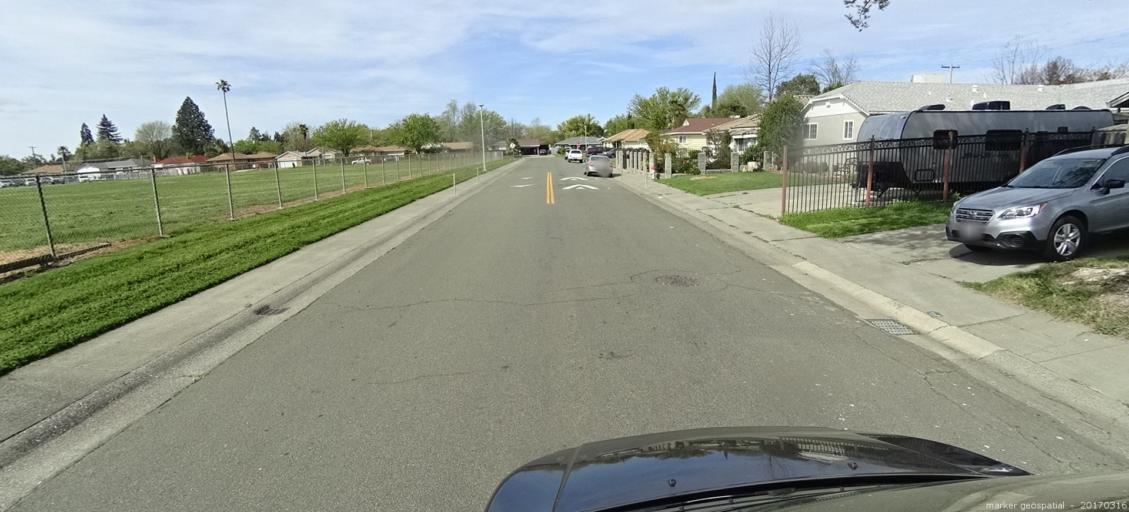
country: US
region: California
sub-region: Sacramento County
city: Parkway
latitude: 38.5044
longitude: -121.4882
